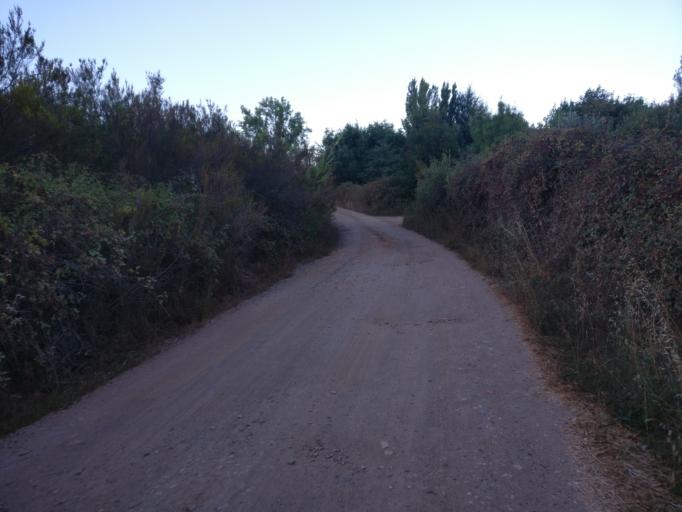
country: PT
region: Beja
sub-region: Odemira
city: Odemira
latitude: 37.7121
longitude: -8.5163
